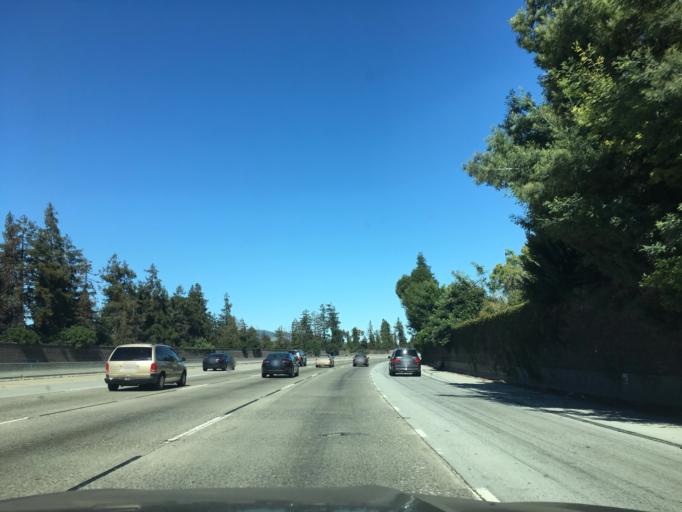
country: US
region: California
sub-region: Santa Clara County
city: Cupertino
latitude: 37.3182
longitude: -121.9884
